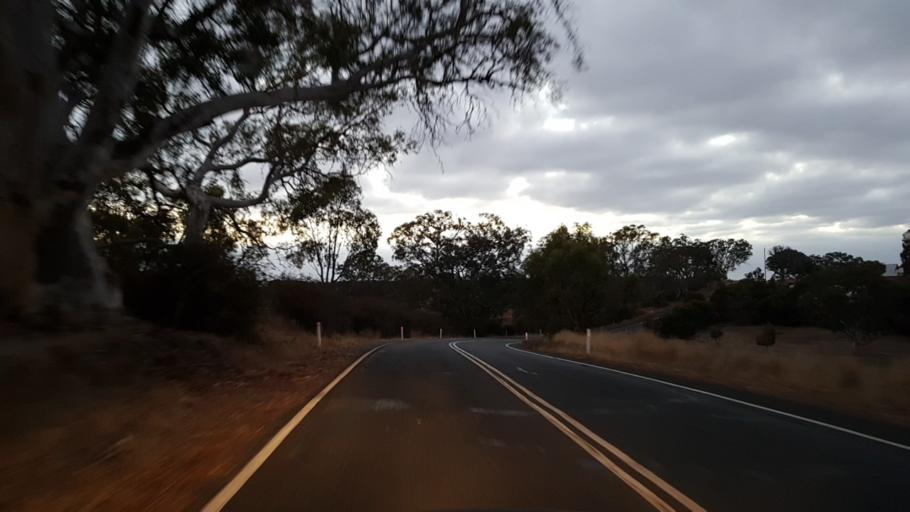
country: AU
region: South Australia
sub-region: Mount Barker
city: Nairne
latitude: -35.0305
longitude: 138.9565
